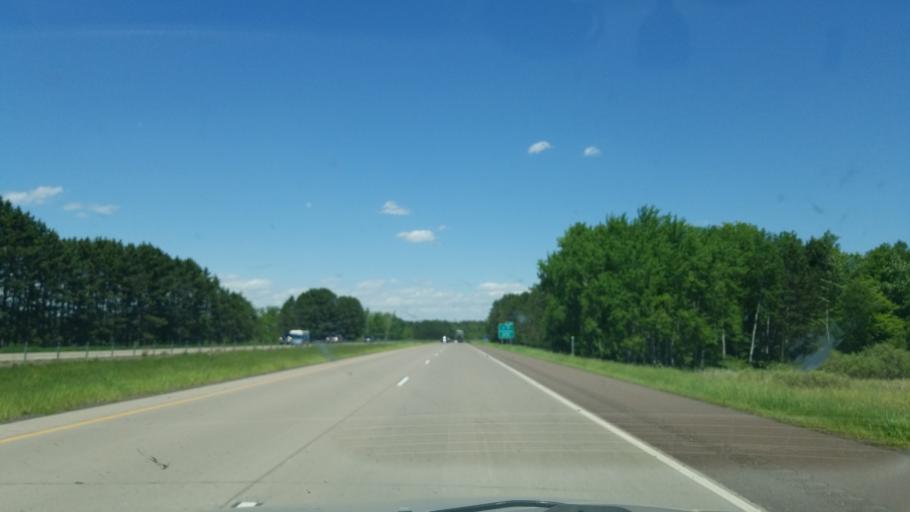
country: US
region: Minnesota
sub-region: Pine County
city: Sandstone
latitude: 46.1624
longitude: -92.8752
